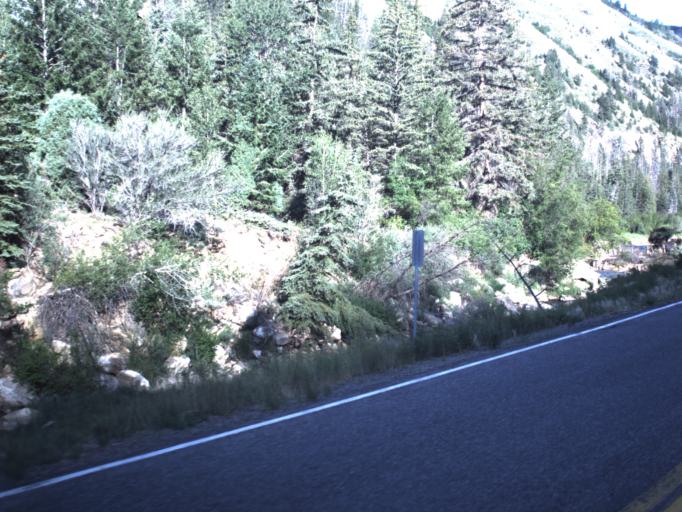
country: US
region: Utah
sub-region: Emery County
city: Huntington
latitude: 39.4642
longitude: -111.1460
